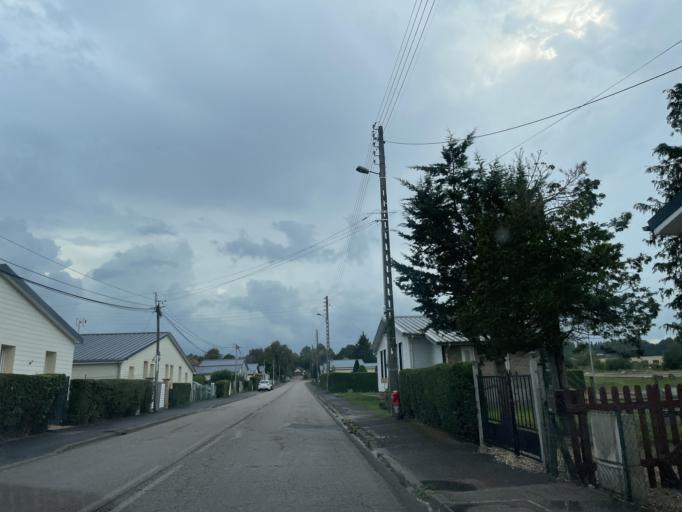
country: FR
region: Haute-Normandie
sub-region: Departement de la Seine-Maritime
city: Neufchatel-en-Bray
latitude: 49.7281
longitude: 1.4391
